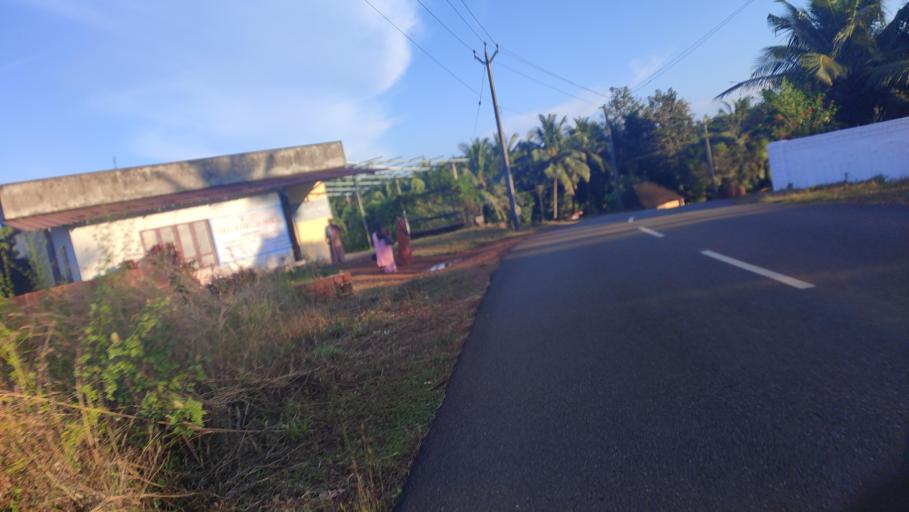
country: IN
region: Kerala
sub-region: Kasaragod District
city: Kasaragod
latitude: 12.4547
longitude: 75.0972
